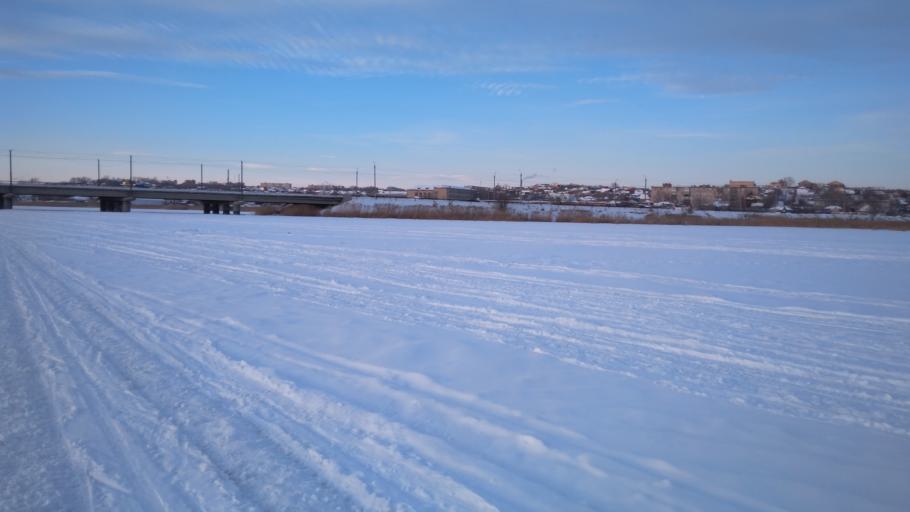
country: RU
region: Chelyabinsk
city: Troitsk
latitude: 54.0901
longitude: 61.5779
